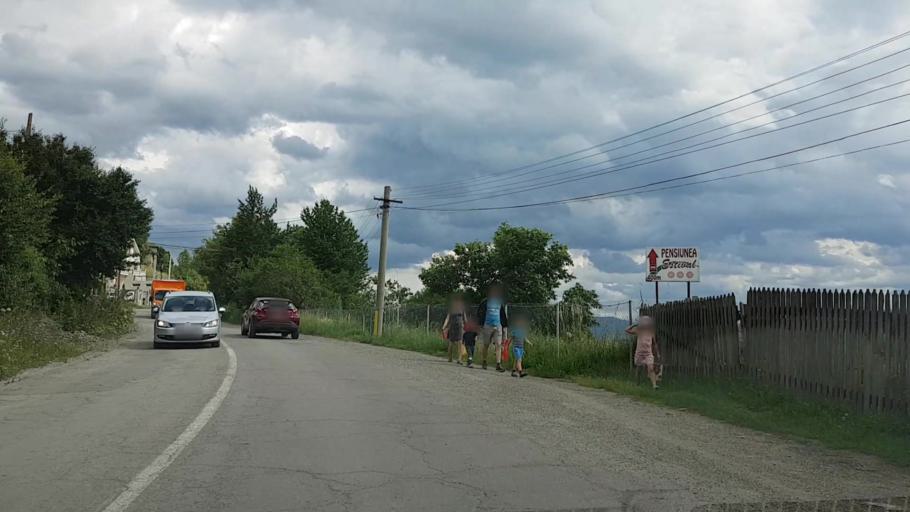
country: RO
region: Neamt
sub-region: Comuna Hangu
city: Hangu
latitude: 47.0474
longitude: 26.0398
